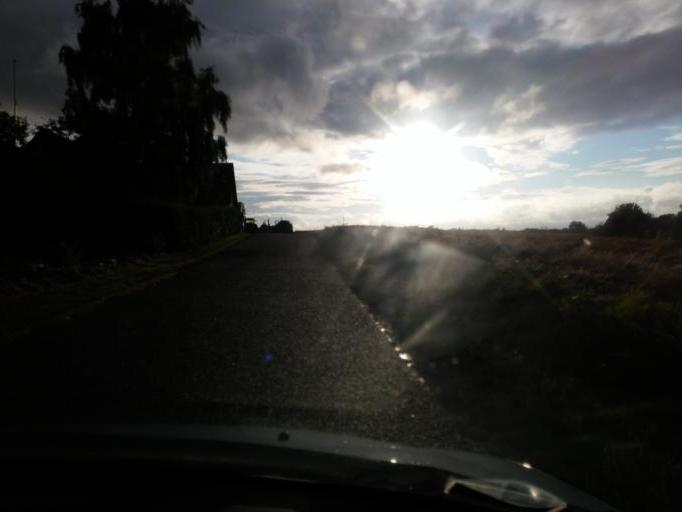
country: DK
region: South Denmark
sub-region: Kerteminde Kommune
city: Munkebo
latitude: 55.5182
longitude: 10.5971
